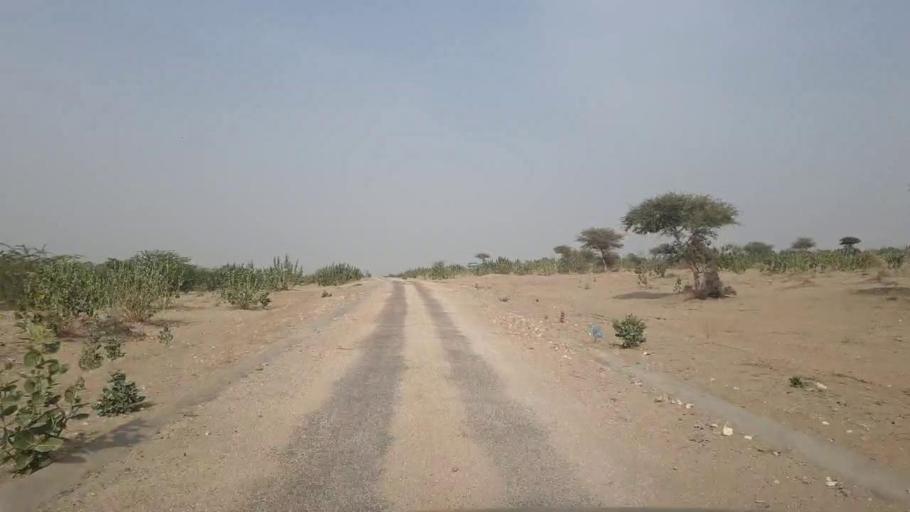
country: PK
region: Sindh
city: Chor
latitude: 25.6435
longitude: 69.9611
